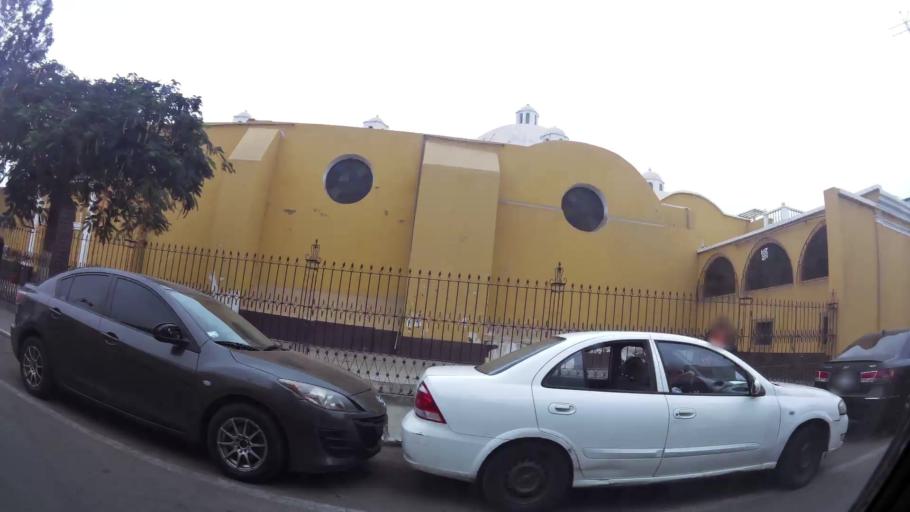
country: PE
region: La Libertad
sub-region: Provincia de Trujillo
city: Trujillo
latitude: -8.1133
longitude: -79.0298
